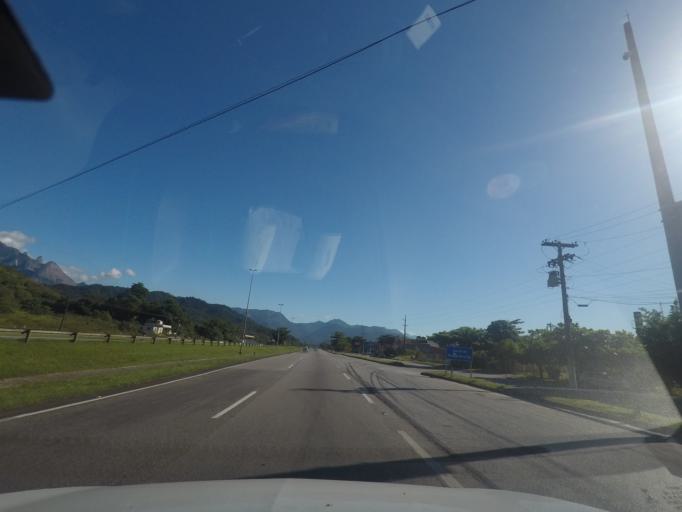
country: BR
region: Rio de Janeiro
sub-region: Guapimirim
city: Guapimirim
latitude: -22.5660
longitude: -43.0006
